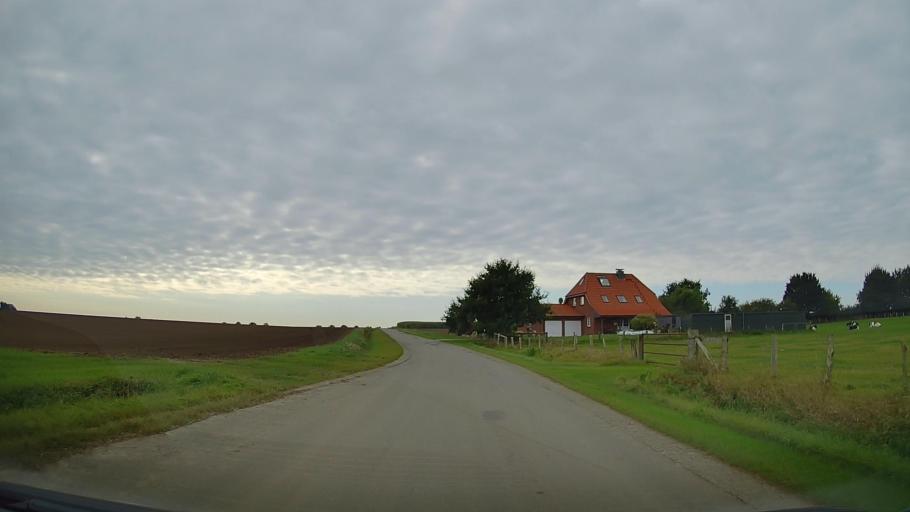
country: DE
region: Schleswig-Holstein
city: Hohenfelde
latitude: 54.3728
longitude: 10.5435
